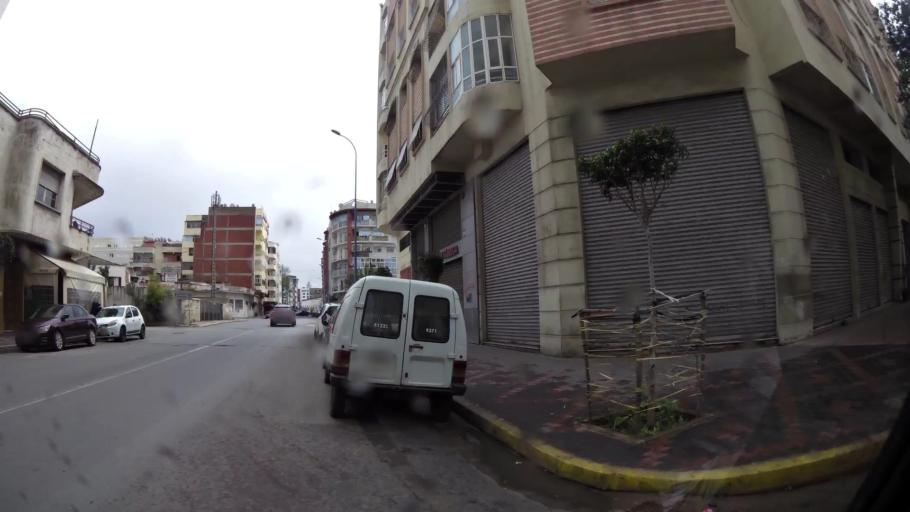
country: MA
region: Grand Casablanca
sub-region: Casablanca
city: Casablanca
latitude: 33.5827
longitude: -7.5987
